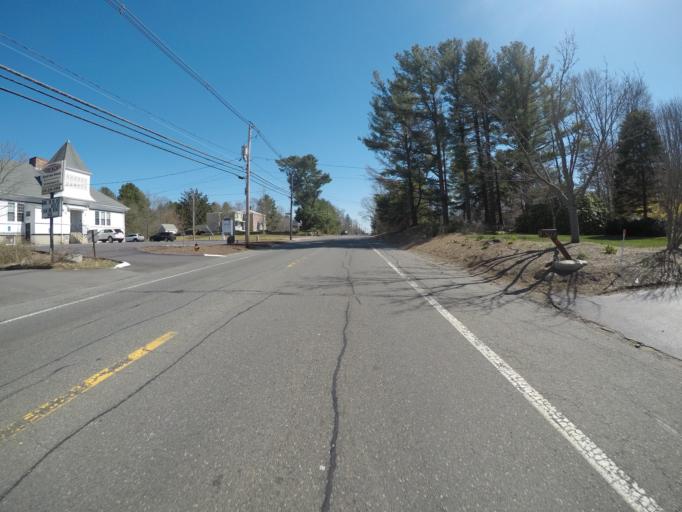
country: US
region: Massachusetts
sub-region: Norfolk County
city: Stoughton
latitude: 42.0803
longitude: -71.0893
